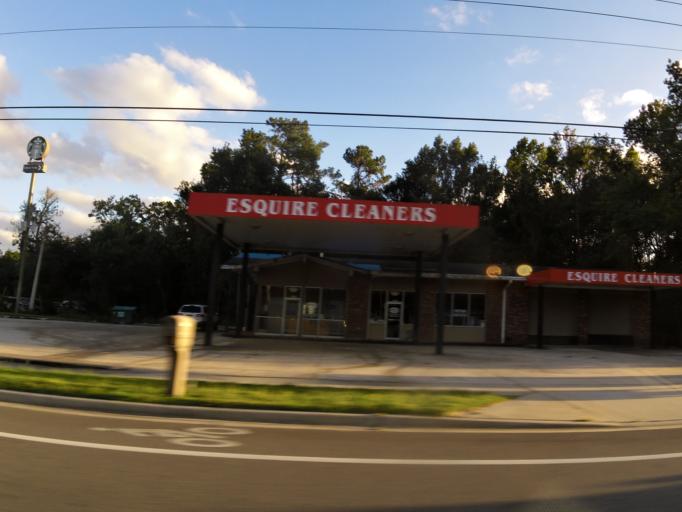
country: US
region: Florida
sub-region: Saint Johns County
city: Fruit Cove
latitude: 30.0648
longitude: -81.5009
